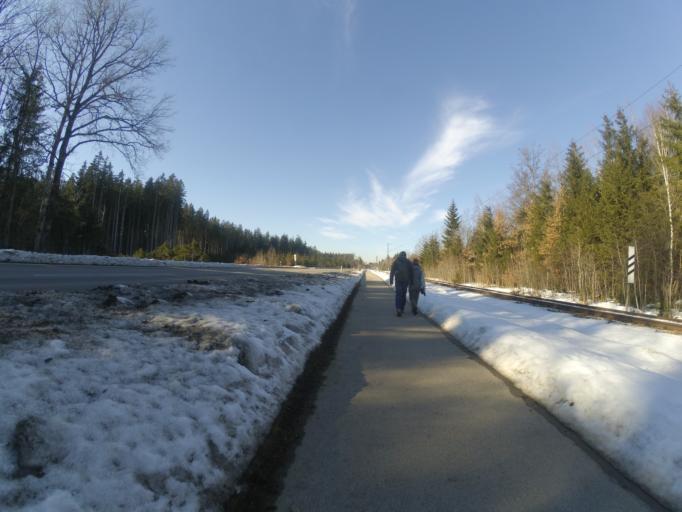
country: DE
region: Bavaria
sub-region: Upper Bavaria
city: Hohenkirchen-Siegertsbrunn
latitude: 48.0016
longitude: 11.7288
